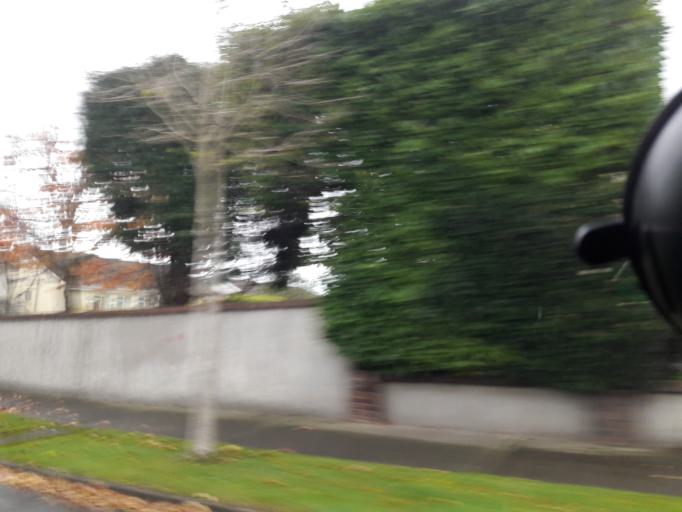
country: IE
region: Leinster
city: Malahide
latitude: 53.4460
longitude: -6.1446
